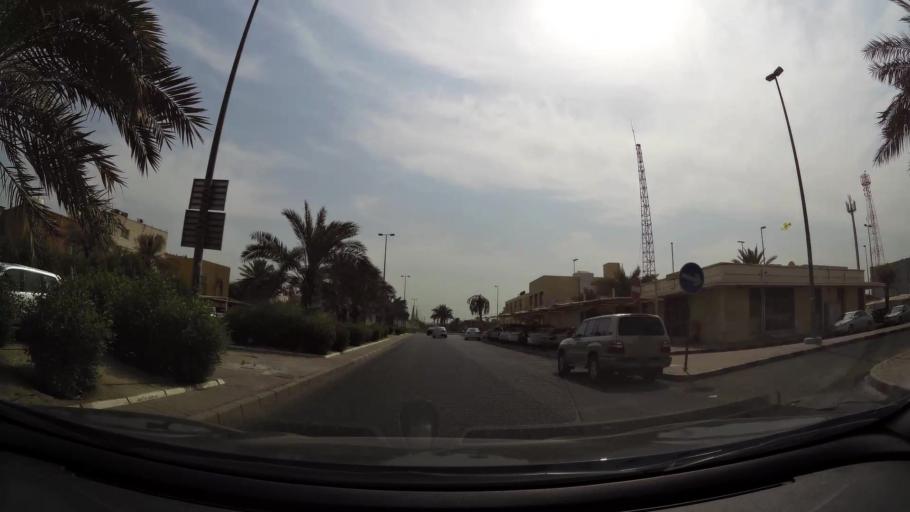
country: KW
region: Al Asimah
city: Ash Shamiyah
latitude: 29.3382
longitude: 47.9810
